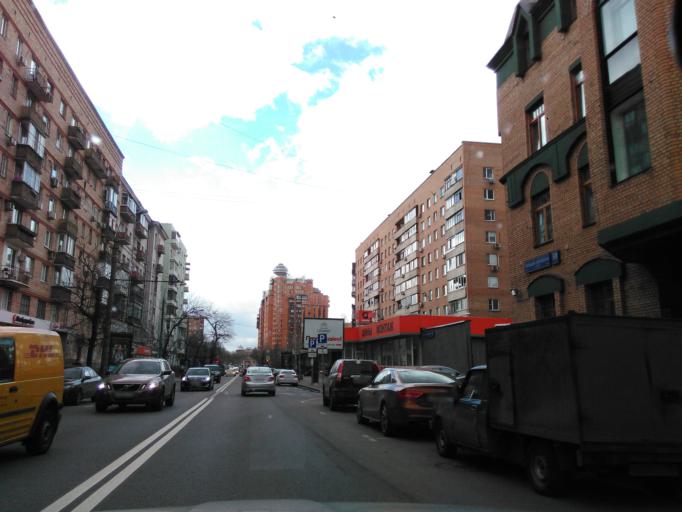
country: RU
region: Moskovskaya
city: Dorogomilovo
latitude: 55.7721
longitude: 37.5845
